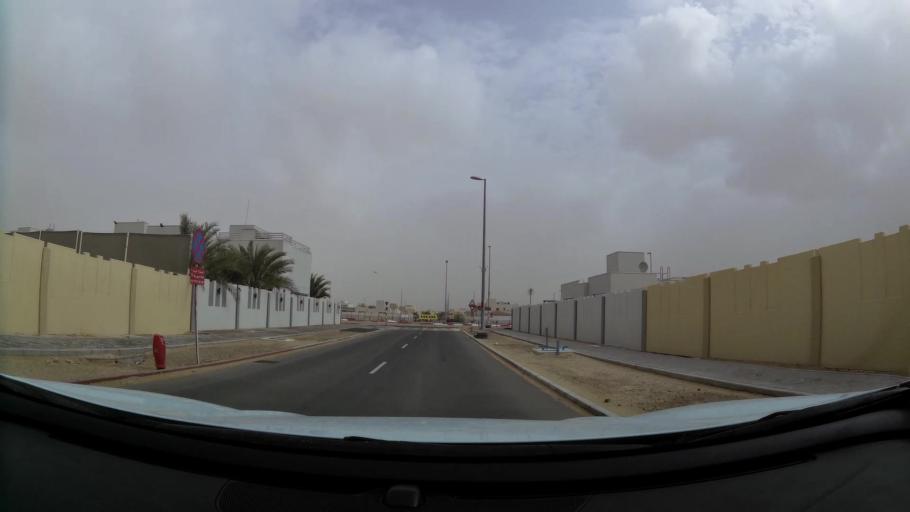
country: AE
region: Abu Dhabi
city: Abu Dhabi
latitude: 24.4535
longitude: 54.7138
